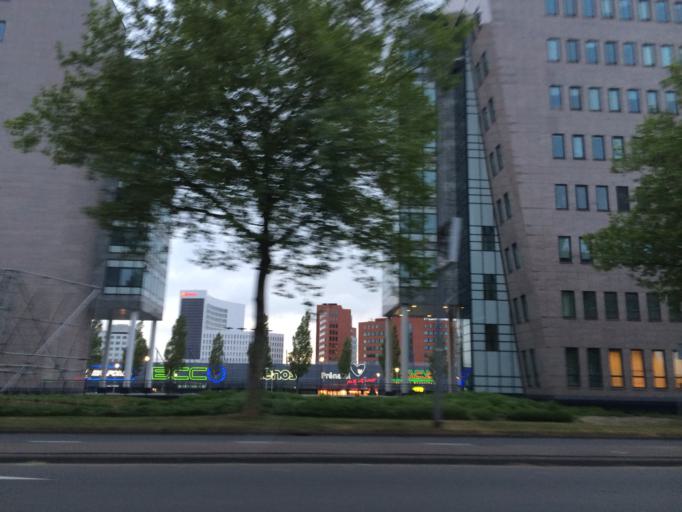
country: NL
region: South Holland
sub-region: Gemeente Rotterdam
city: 's-Gravenland
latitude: 51.9501
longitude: 4.5593
